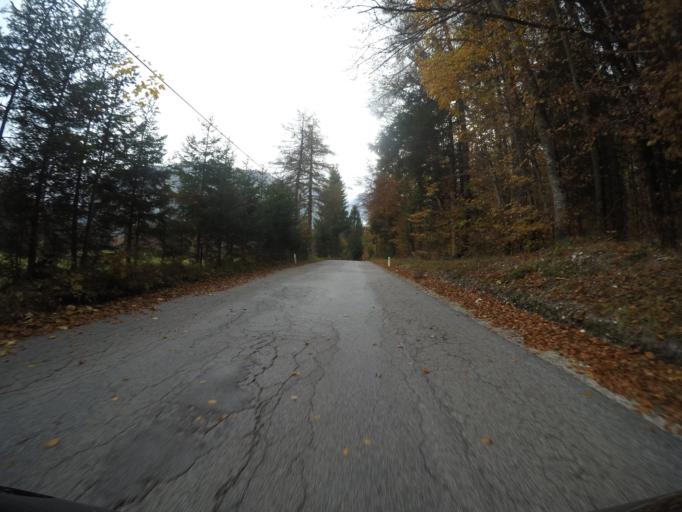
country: SI
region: Kranjska Gora
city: Mojstrana
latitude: 46.4363
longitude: 13.9310
